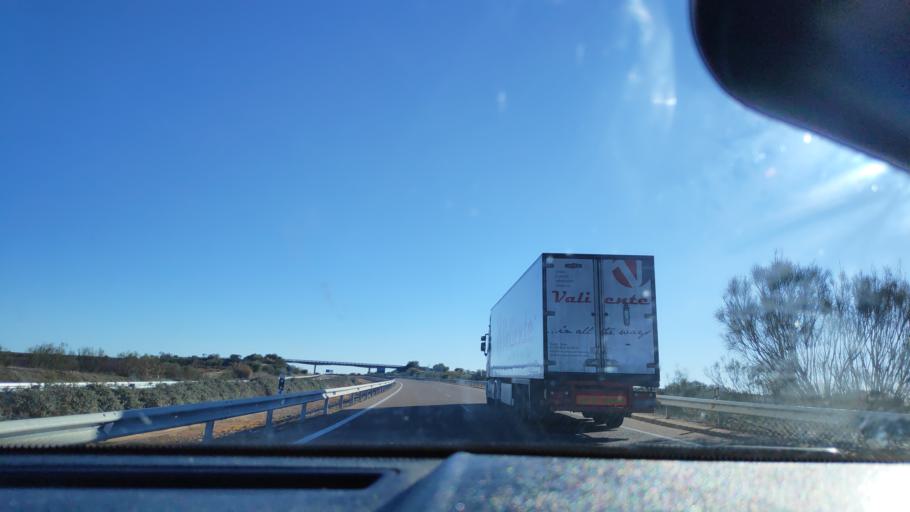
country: ES
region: Extremadura
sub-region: Provincia de Badajoz
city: Los Santos de Maimona
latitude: 38.4312
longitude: -6.3488
